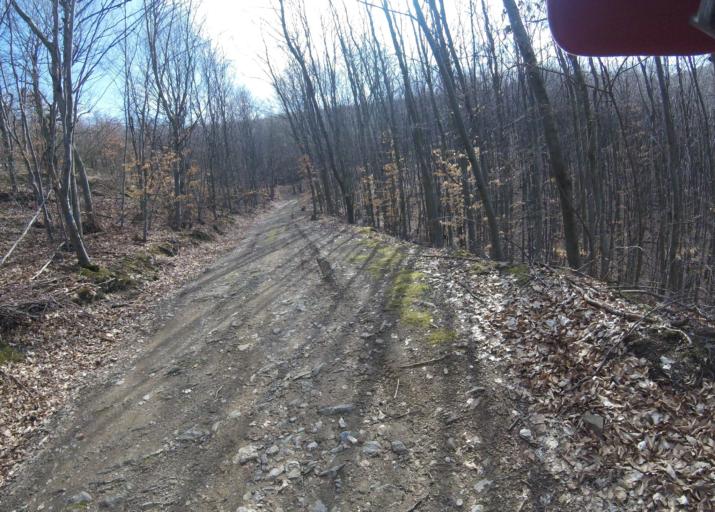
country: HU
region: Heves
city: Belapatfalva
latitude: 48.0291
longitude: 20.3559
